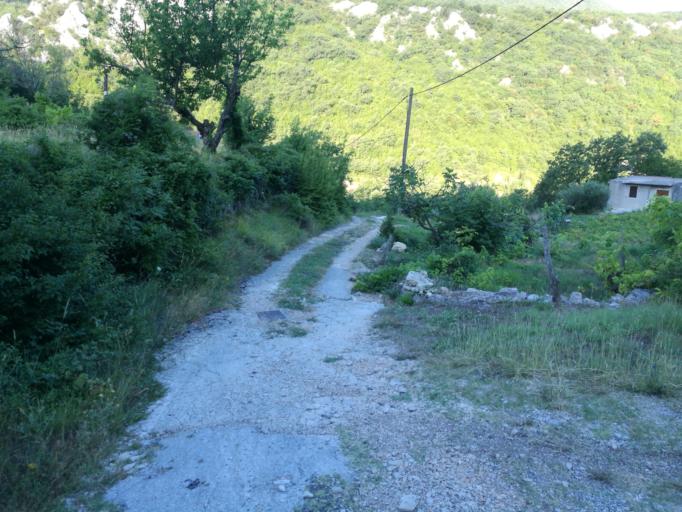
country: HR
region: Splitsko-Dalmatinska
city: Donja Brela
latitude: 43.4228
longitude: 16.8535
